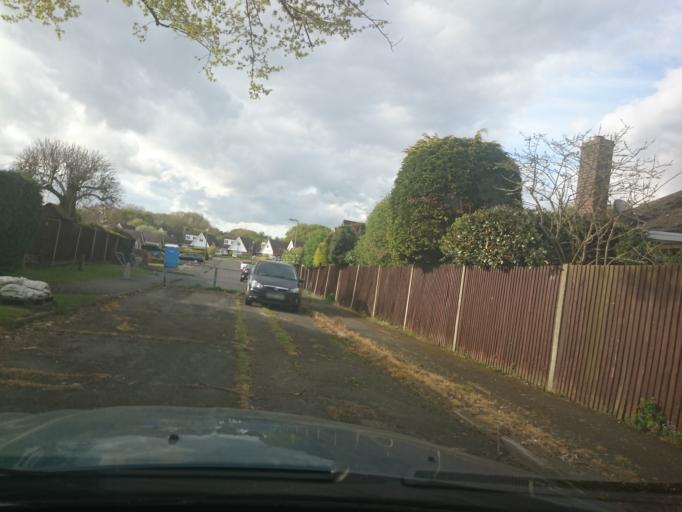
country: GB
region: England
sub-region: Surrey
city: Seale
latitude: 51.2379
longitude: -0.7035
